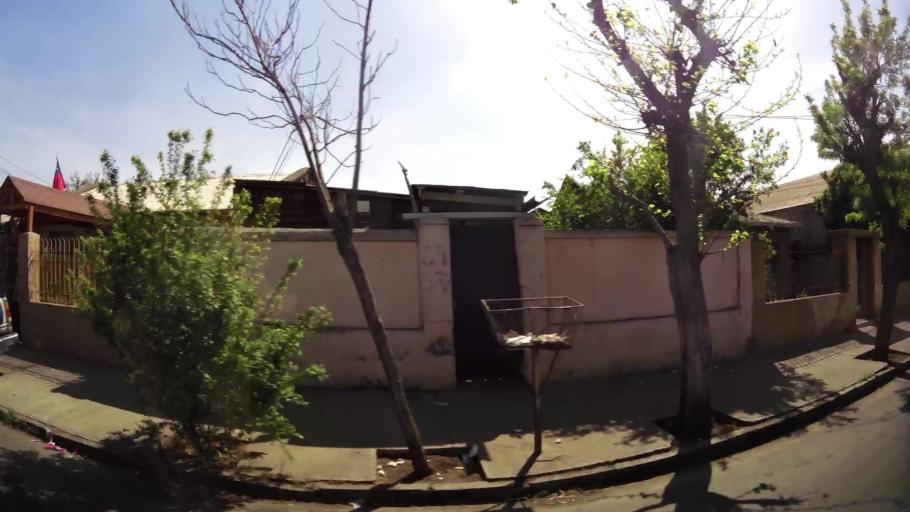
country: CL
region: Santiago Metropolitan
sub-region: Provincia de Maipo
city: San Bernardo
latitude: -33.5362
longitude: -70.6756
